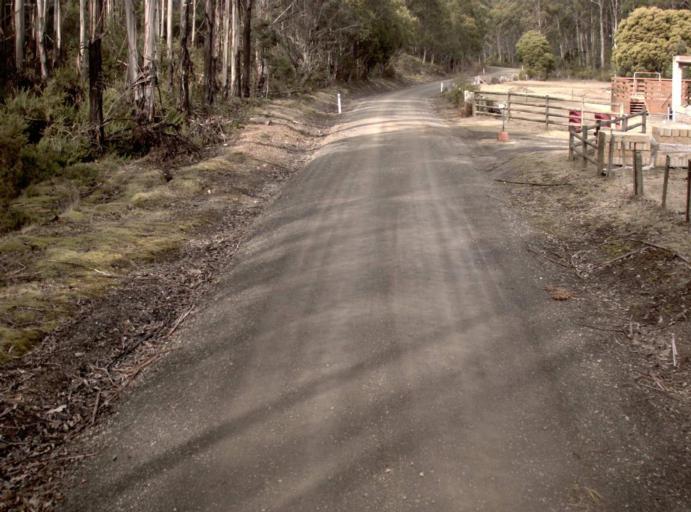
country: AU
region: Tasmania
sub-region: Northern Midlands
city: Evandale
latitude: -41.4530
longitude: 147.4818
